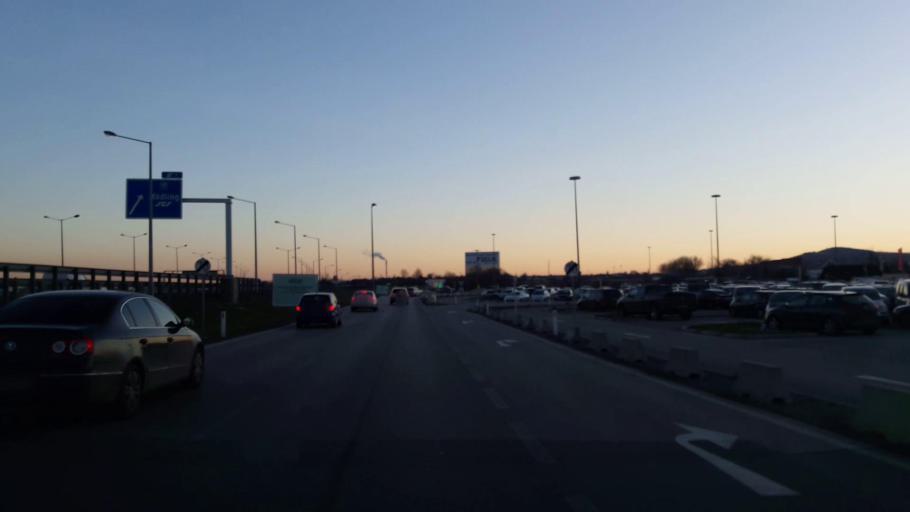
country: AT
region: Lower Austria
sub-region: Politischer Bezirk Modling
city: Wiener Neudorf
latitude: 48.1030
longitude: 16.3199
